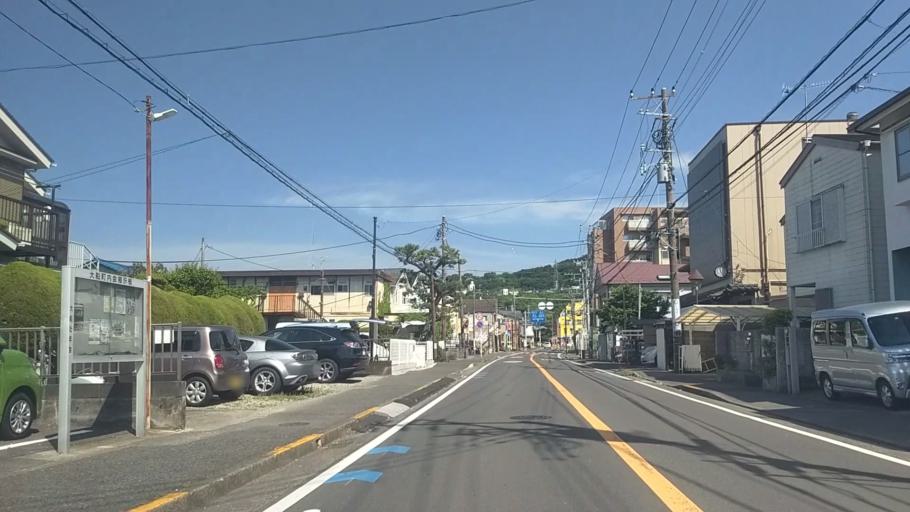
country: JP
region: Kanagawa
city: Kamakura
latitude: 35.3473
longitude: 139.5396
